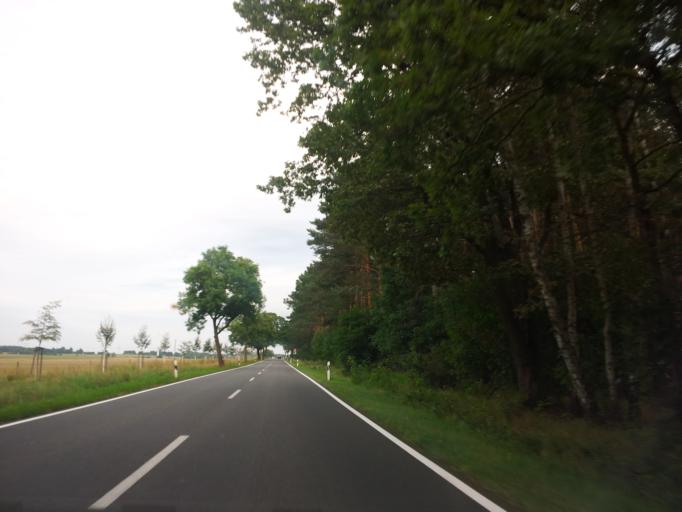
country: DE
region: Brandenburg
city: Treuenbrietzen
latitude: 52.0948
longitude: 12.8197
